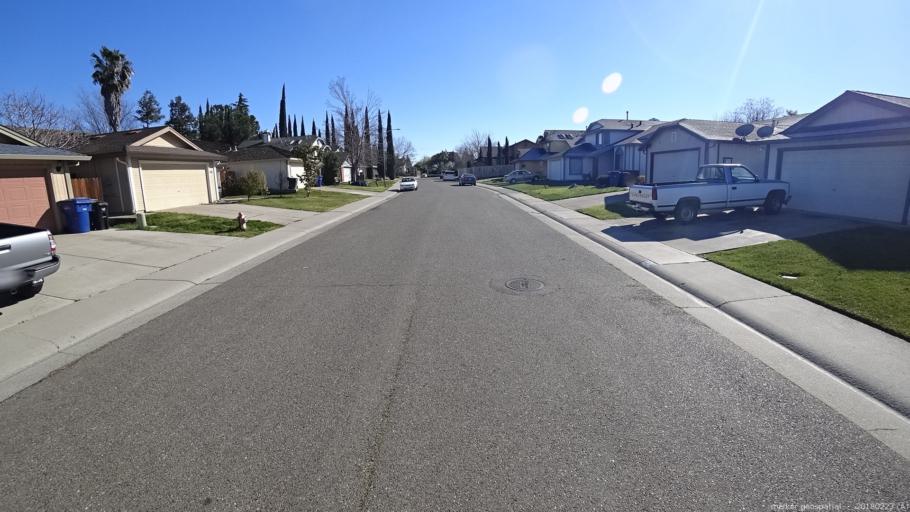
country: US
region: California
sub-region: Sacramento County
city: North Highlands
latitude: 38.7068
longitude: -121.3662
